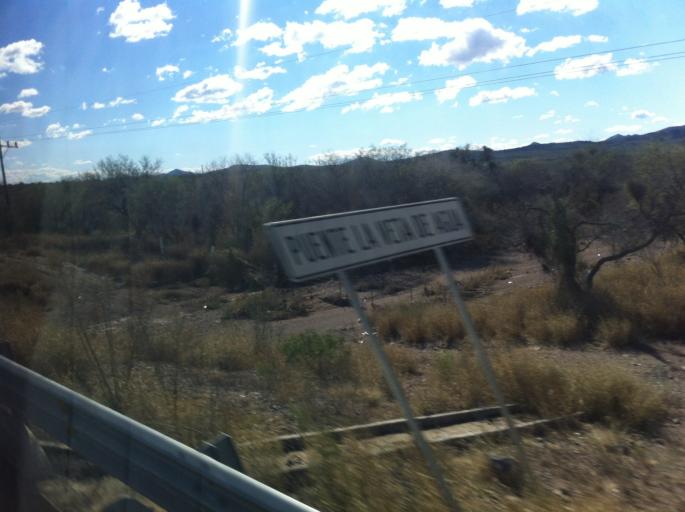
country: MX
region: Sonora
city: Santa Ana
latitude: 30.4675
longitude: -111.0911
